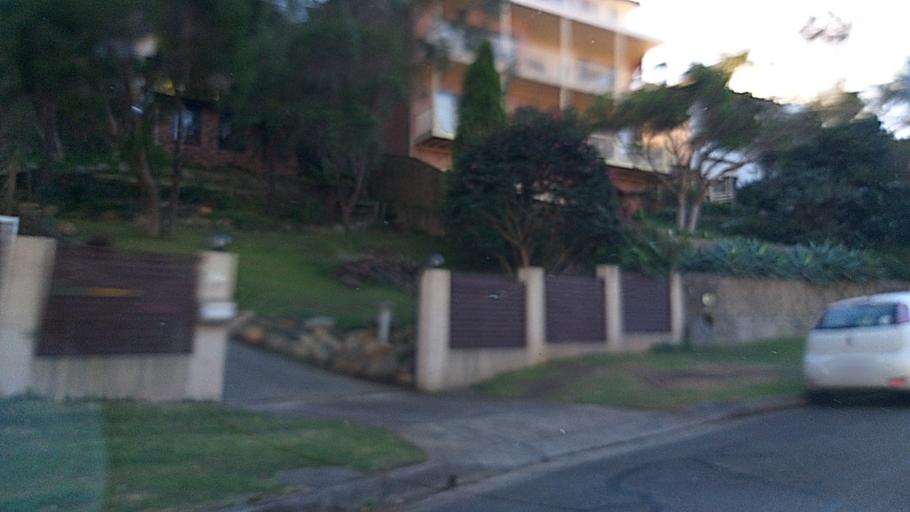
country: AU
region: New South Wales
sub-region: Wollongong
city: Bulli
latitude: -34.3347
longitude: 150.9062
